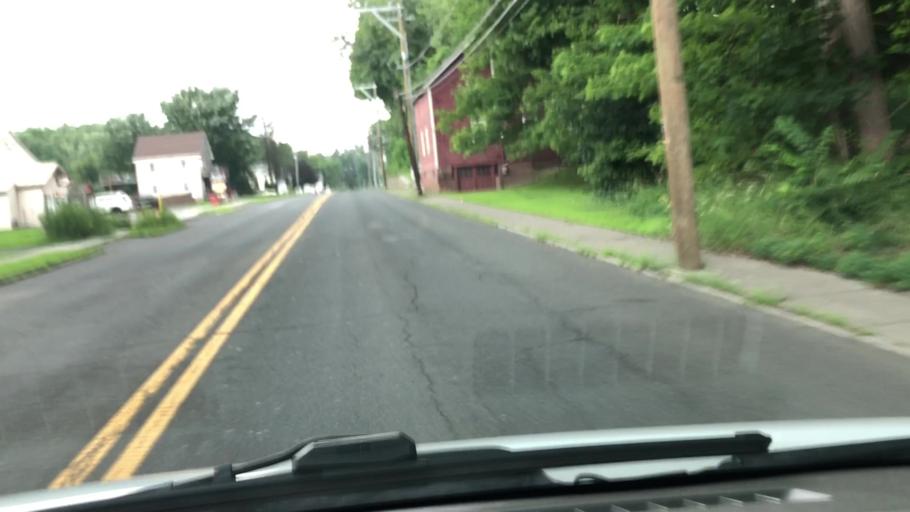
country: US
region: Massachusetts
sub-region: Franklin County
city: Greenfield
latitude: 42.5738
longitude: -72.5965
